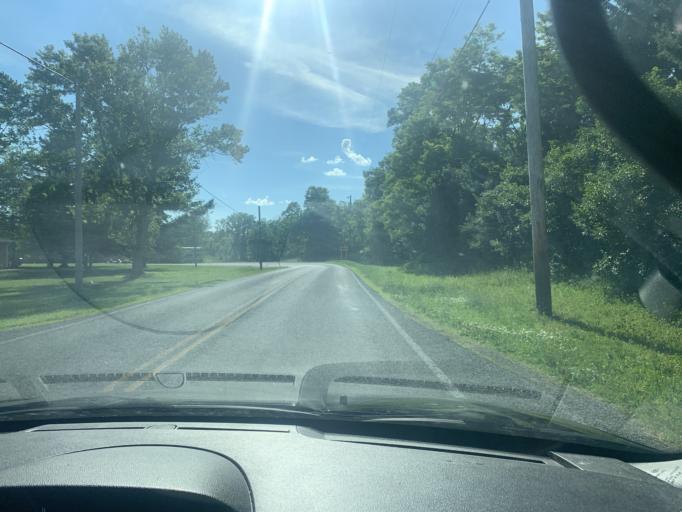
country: US
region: Ohio
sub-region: Logan County
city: Bellefontaine
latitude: 40.3503
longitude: -83.8166
